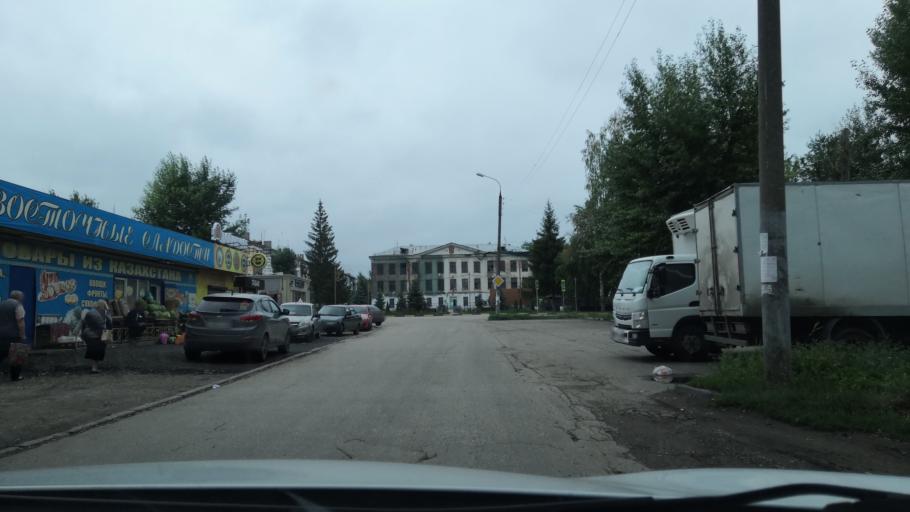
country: RU
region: Samara
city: Smyshlyayevka
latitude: 53.2696
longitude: 50.3944
